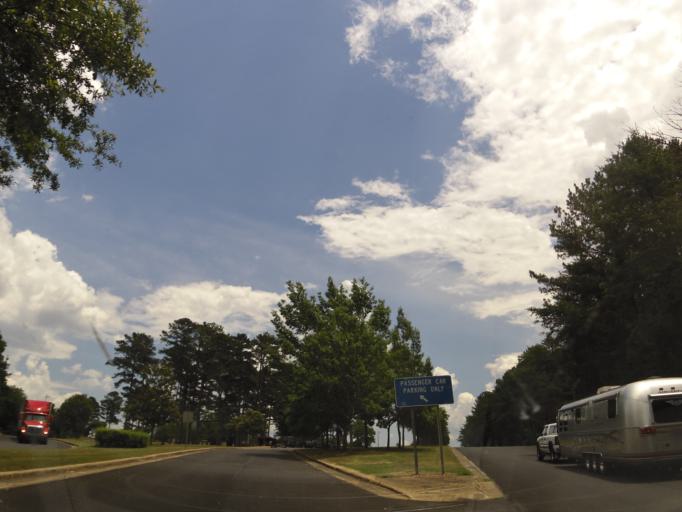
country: US
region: Alabama
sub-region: Sumter County
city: York
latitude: 32.4493
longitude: -88.3988
